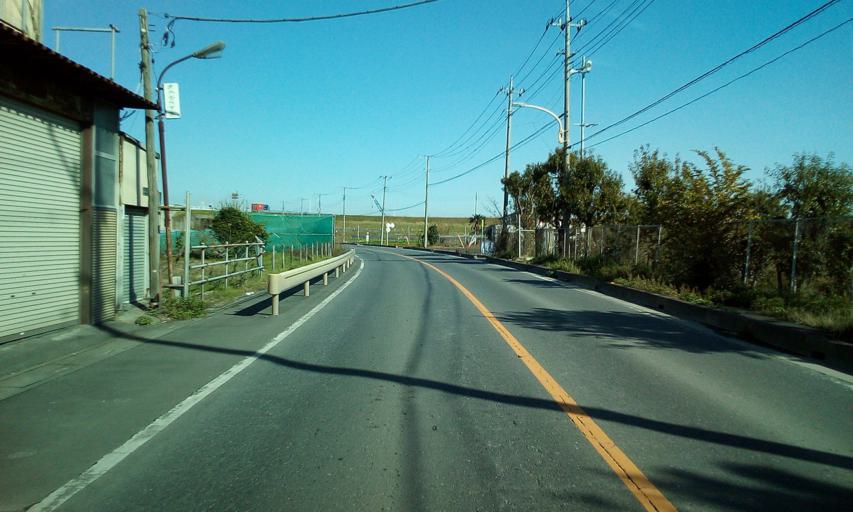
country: JP
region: Chiba
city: Noda
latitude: 35.9103
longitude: 139.8689
